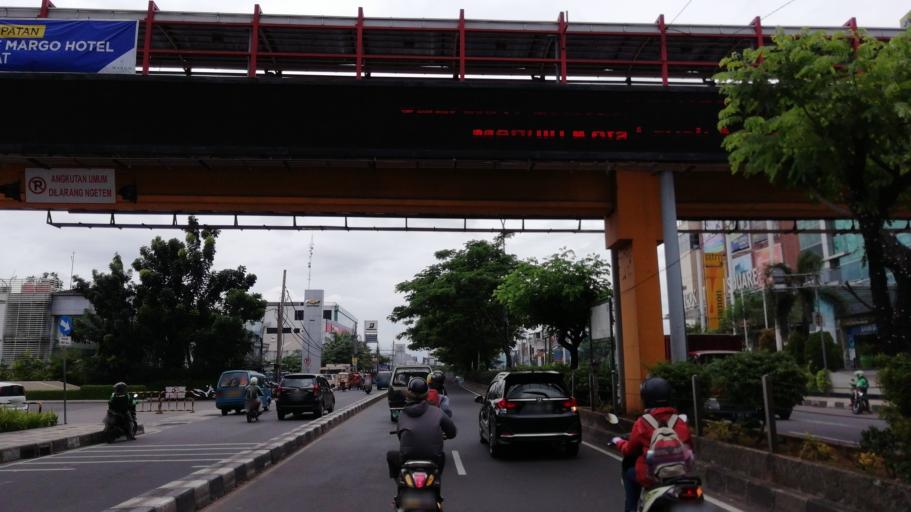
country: ID
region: West Java
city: Depok
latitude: -6.3722
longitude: 106.8330
